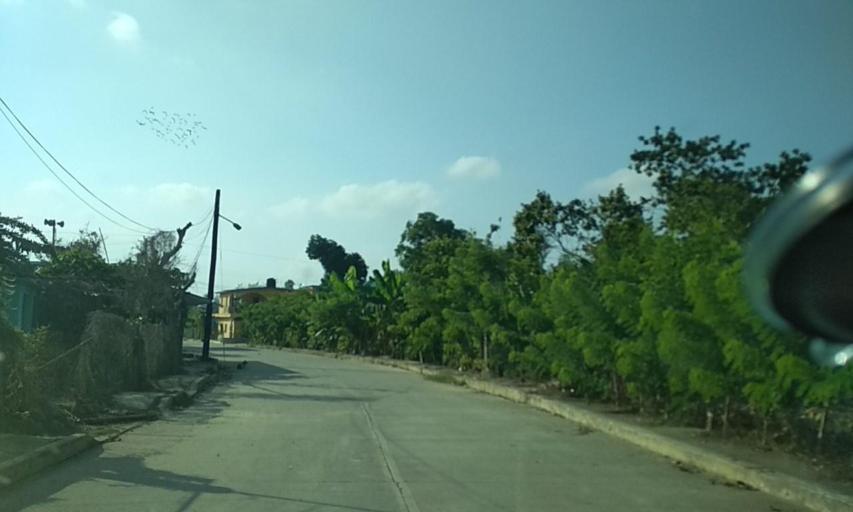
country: MX
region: Veracruz
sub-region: Papantla
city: Polutla
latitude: 20.5978
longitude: -97.2560
